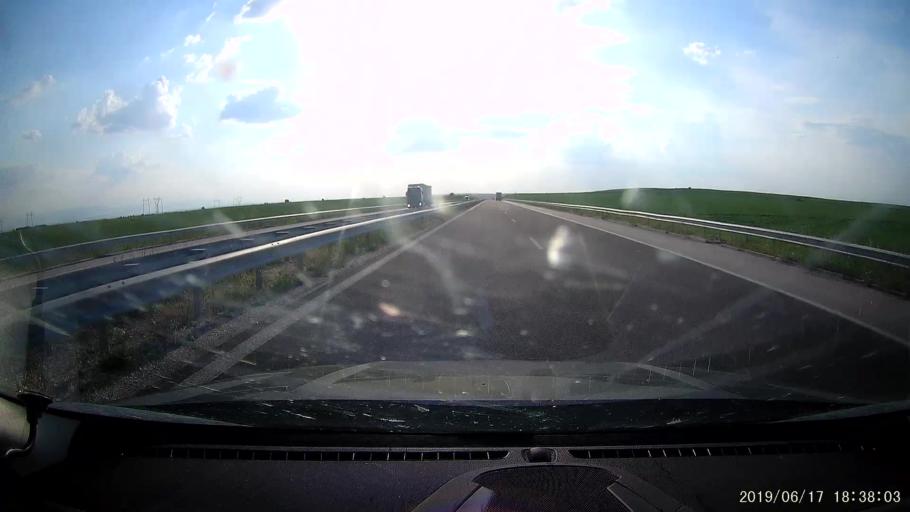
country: BG
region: Stara Zagora
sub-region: Obshtina Chirpan
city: Chirpan
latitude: 42.1349
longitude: 25.3463
